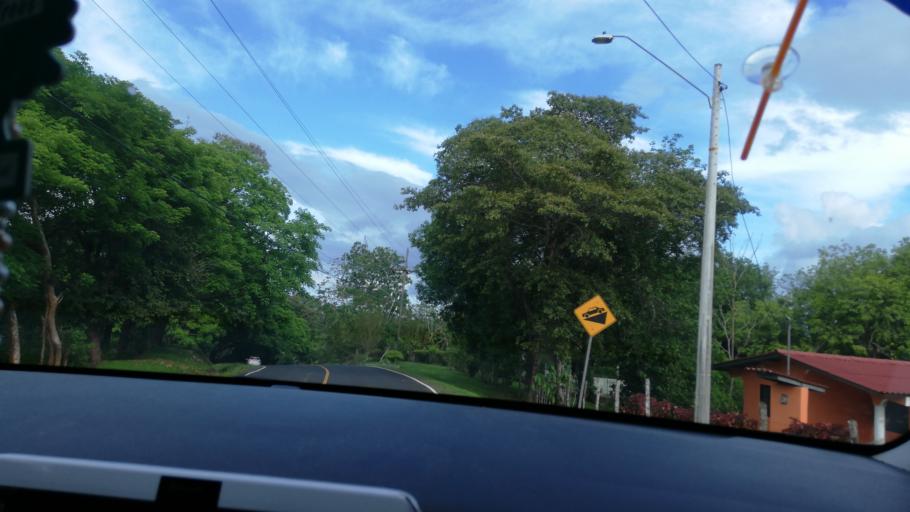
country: PA
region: Panama
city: Las Colinas
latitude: 8.4920
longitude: -80.0243
